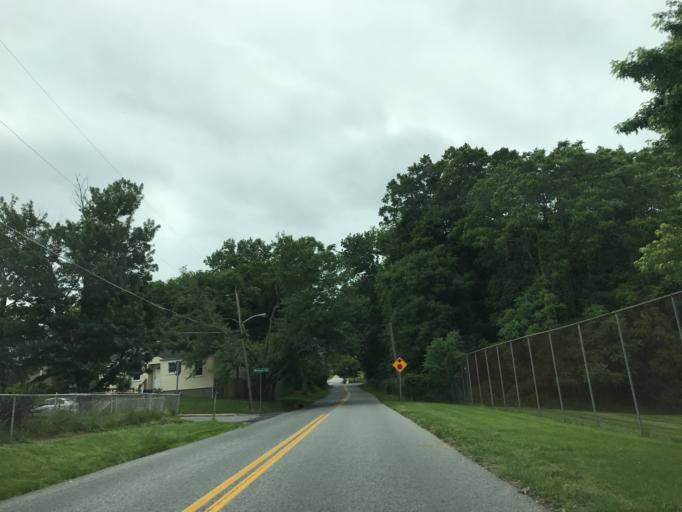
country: US
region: Maryland
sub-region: Baltimore County
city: Arbutus
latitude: 39.2476
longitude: -76.7074
